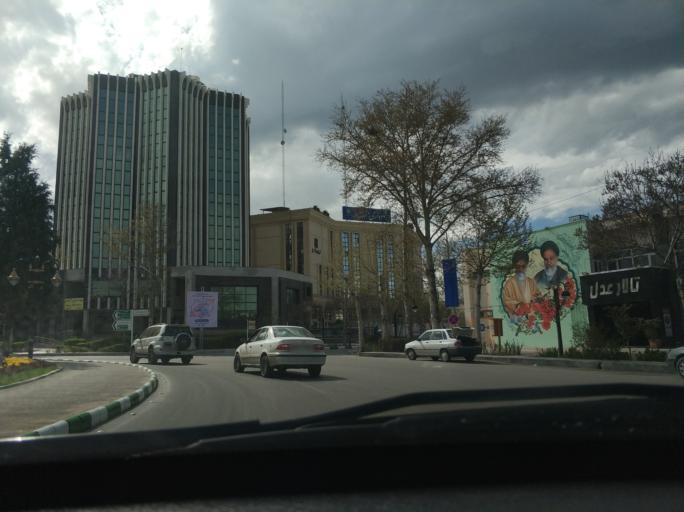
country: IR
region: Razavi Khorasan
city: Mashhad
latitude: 36.2753
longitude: 59.5920
